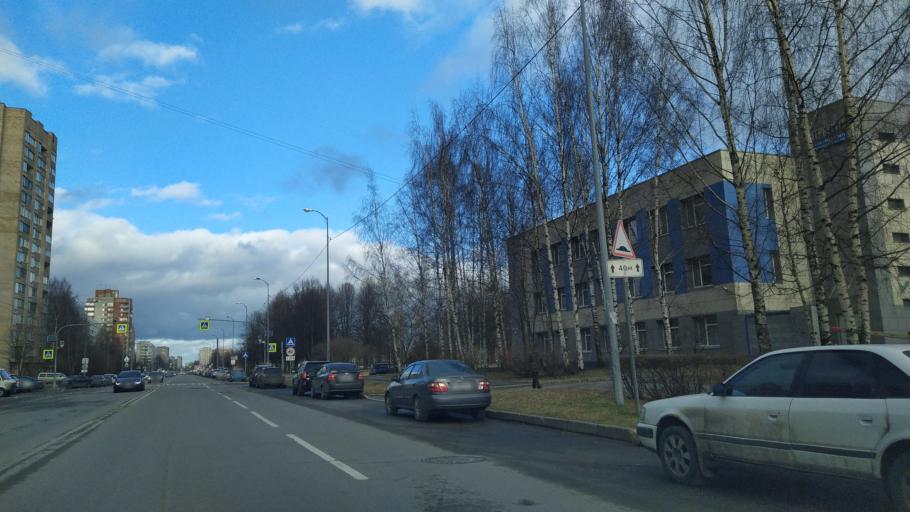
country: RU
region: St.-Petersburg
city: Grazhdanka
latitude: 60.0376
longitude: 30.3827
